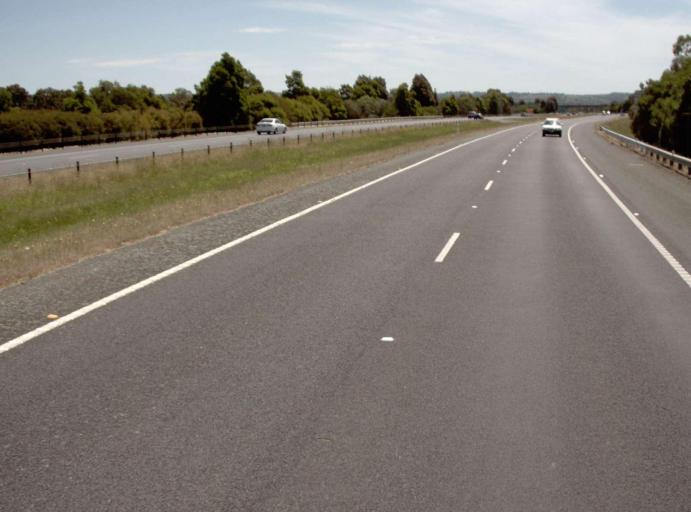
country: AU
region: Victoria
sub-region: Latrobe
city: Morwell
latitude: -38.2401
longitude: 146.3848
